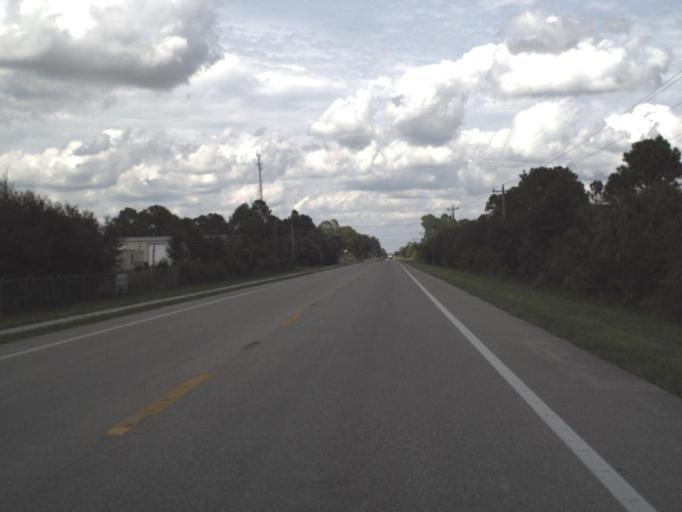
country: US
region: Florida
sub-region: Collier County
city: Immokalee
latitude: 26.5489
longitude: -81.4357
